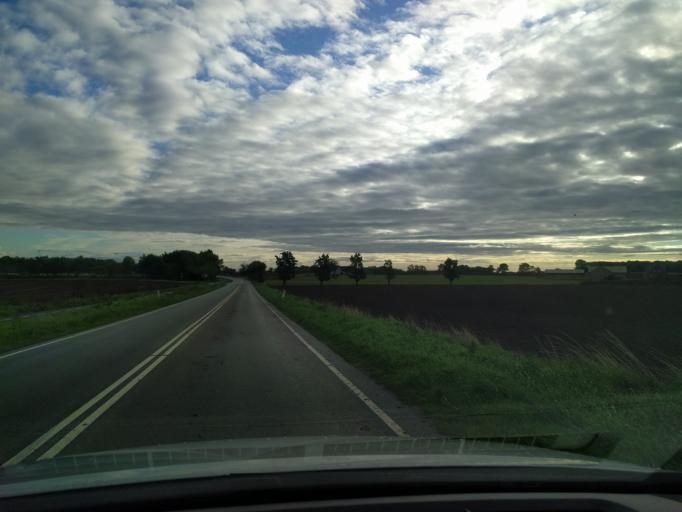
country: DK
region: South Denmark
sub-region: Kerteminde Kommune
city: Langeskov
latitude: 55.4059
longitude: 10.5893
